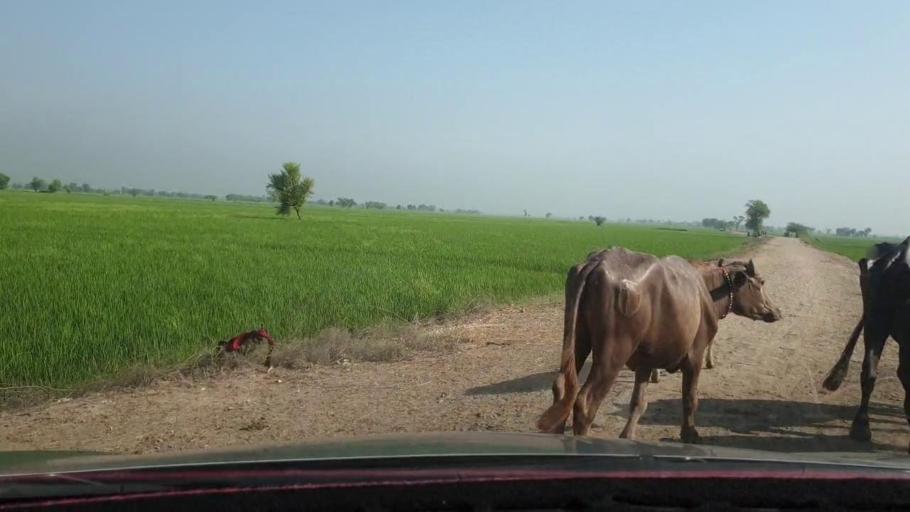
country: PK
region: Sindh
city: Nasirabad
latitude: 27.4650
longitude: 67.9202
